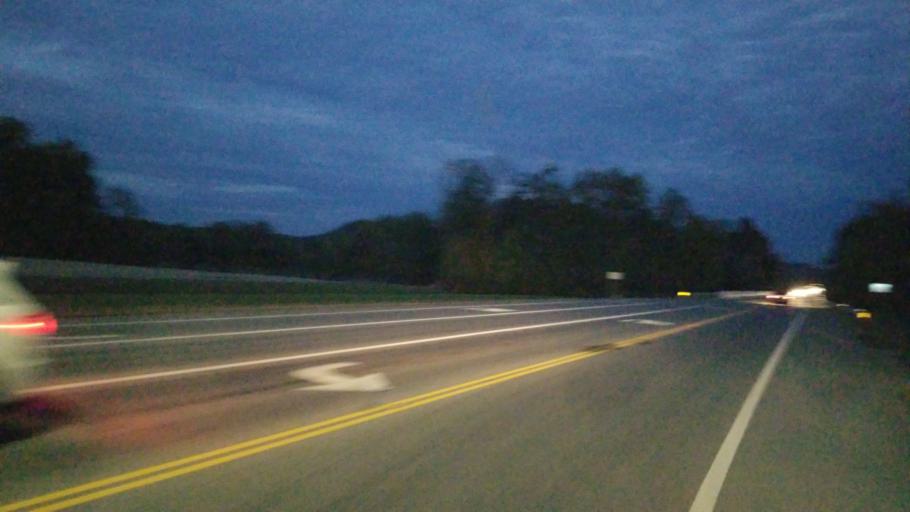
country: US
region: Ohio
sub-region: Scioto County
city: Lucasville
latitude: 38.8809
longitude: -83.0196
